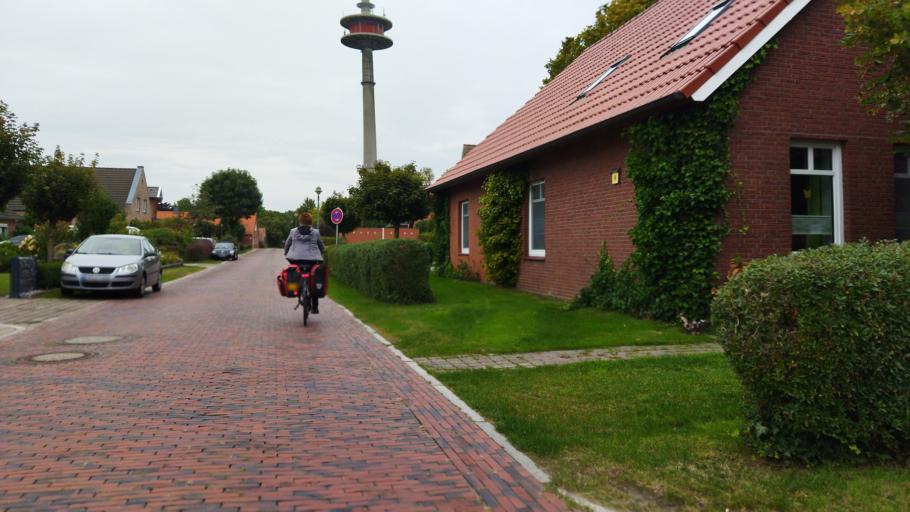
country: DE
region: Lower Saxony
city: Leer
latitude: 53.2612
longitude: 7.4353
